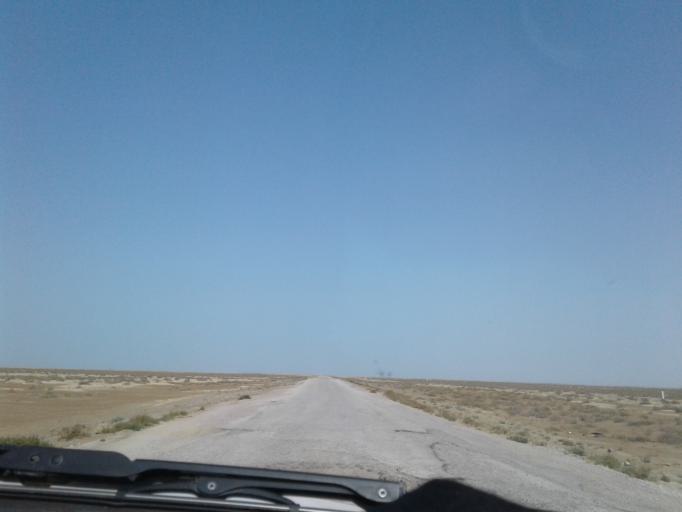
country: IR
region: Golestan
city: Gomishan
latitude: 37.9083
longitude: 53.8561
